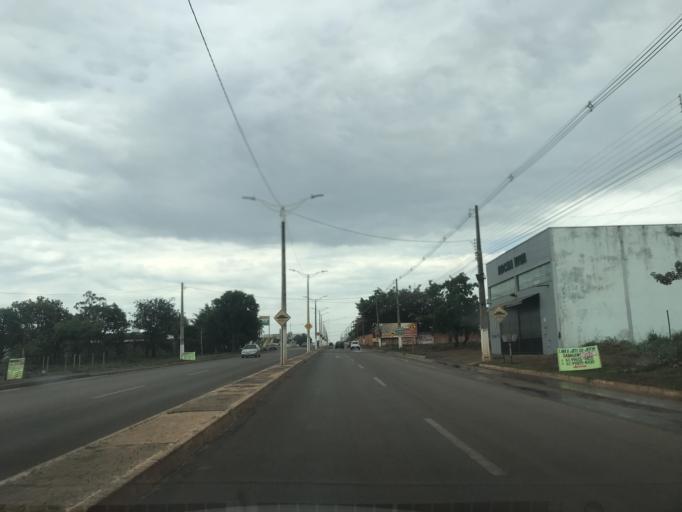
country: BR
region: Goias
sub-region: Luziania
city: Luziania
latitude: -16.2223
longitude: -47.9354
